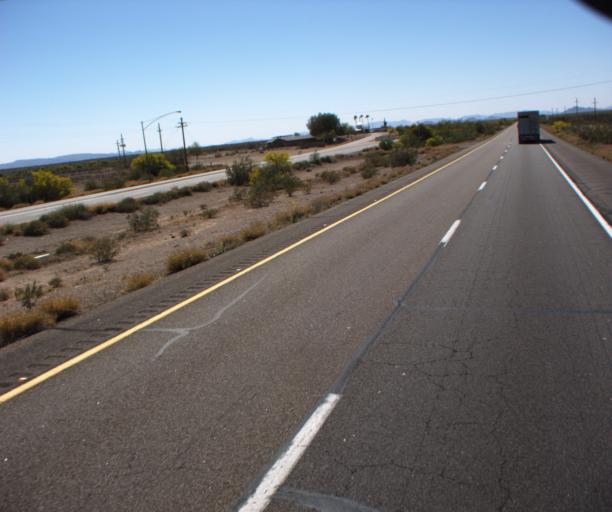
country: US
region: Arizona
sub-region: Maricopa County
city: Gila Bend
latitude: 32.8515
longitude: -113.2615
